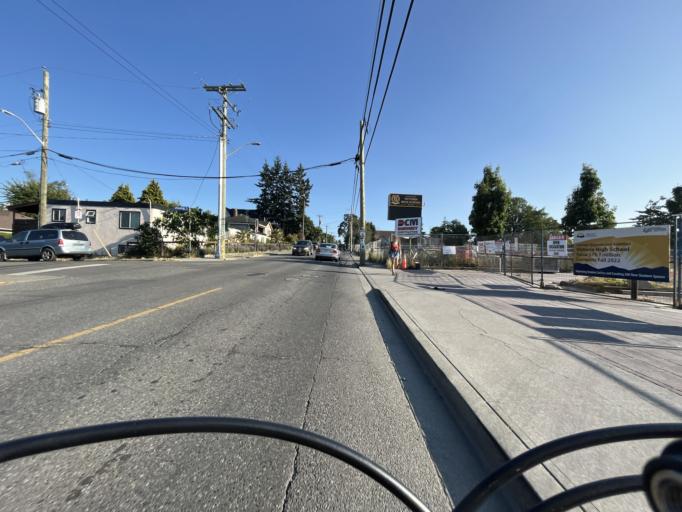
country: CA
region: British Columbia
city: Victoria
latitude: 48.4297
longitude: -123.3453
